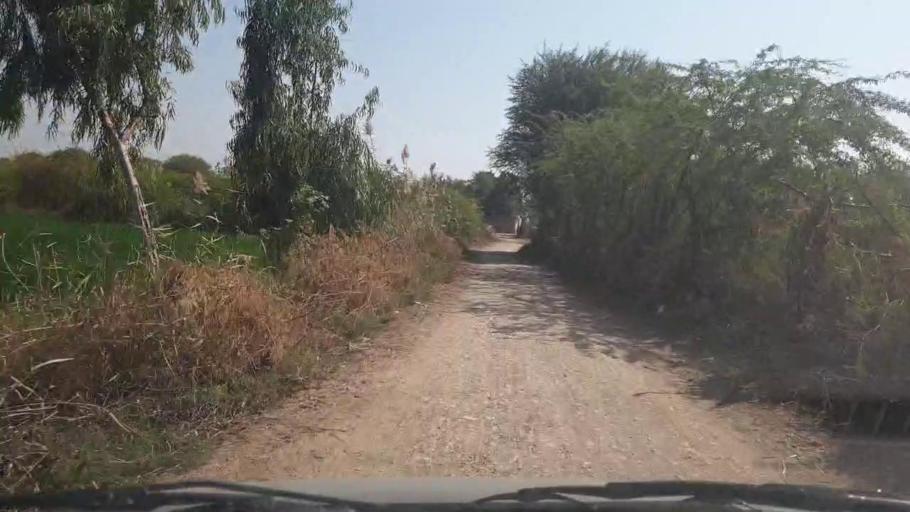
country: PK
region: Sindh
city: Samaro
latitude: 25.2639
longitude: 69.3438
